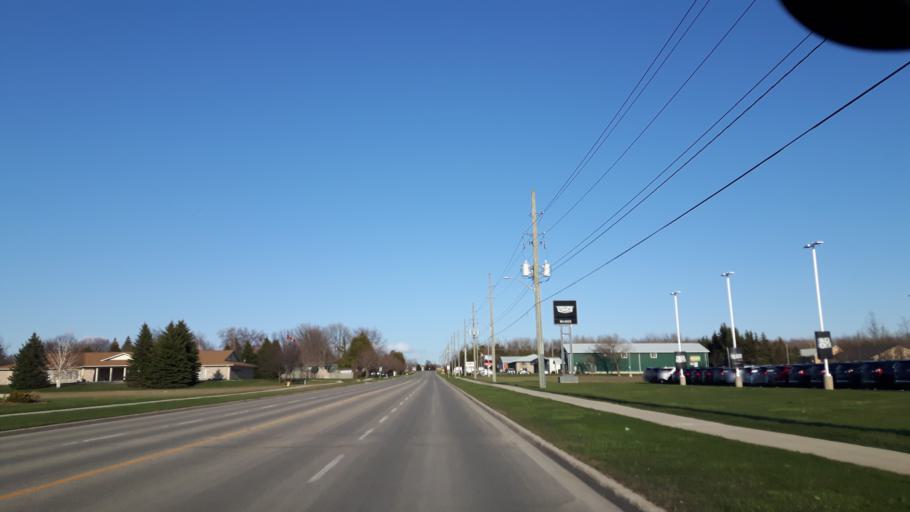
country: CA
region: Ontario
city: Goderich
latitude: 43.7316
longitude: -81.7031
